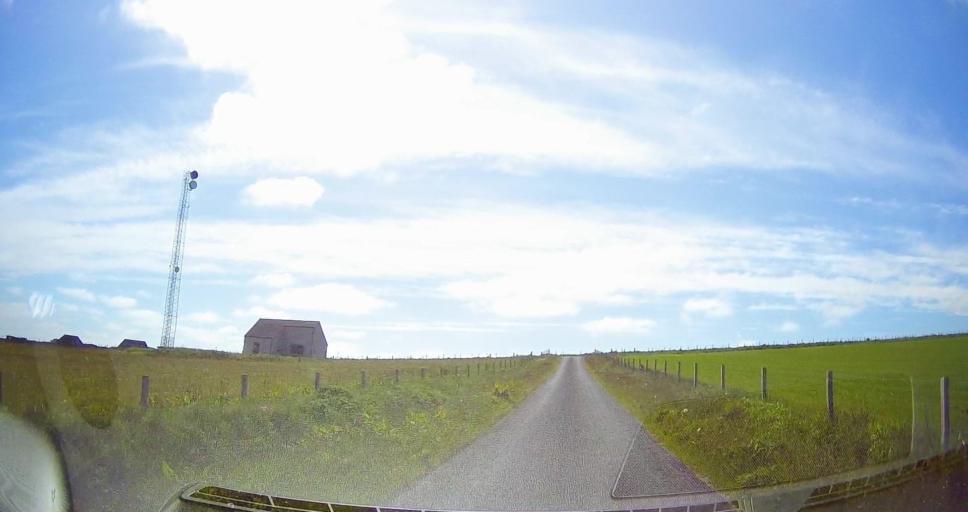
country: GB
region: Scotland
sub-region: Orkney Islands
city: Kirkwall
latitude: 58.8378
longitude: -2.9074
